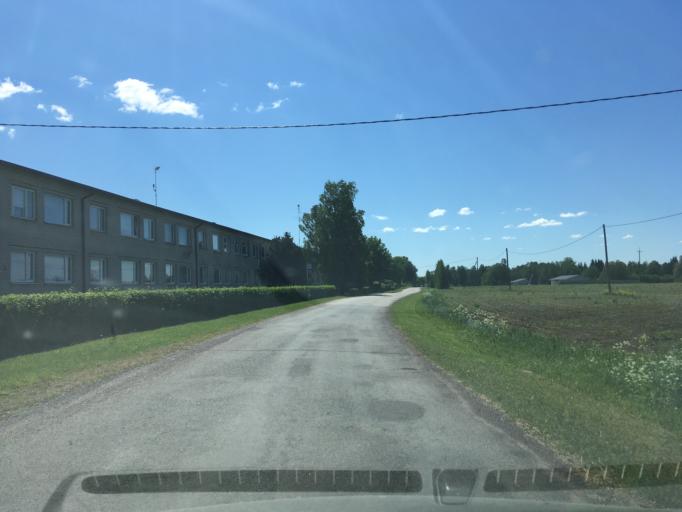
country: EE
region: Harju
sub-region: Rae vald
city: Vaida
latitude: 59.1669
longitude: 25.1246
